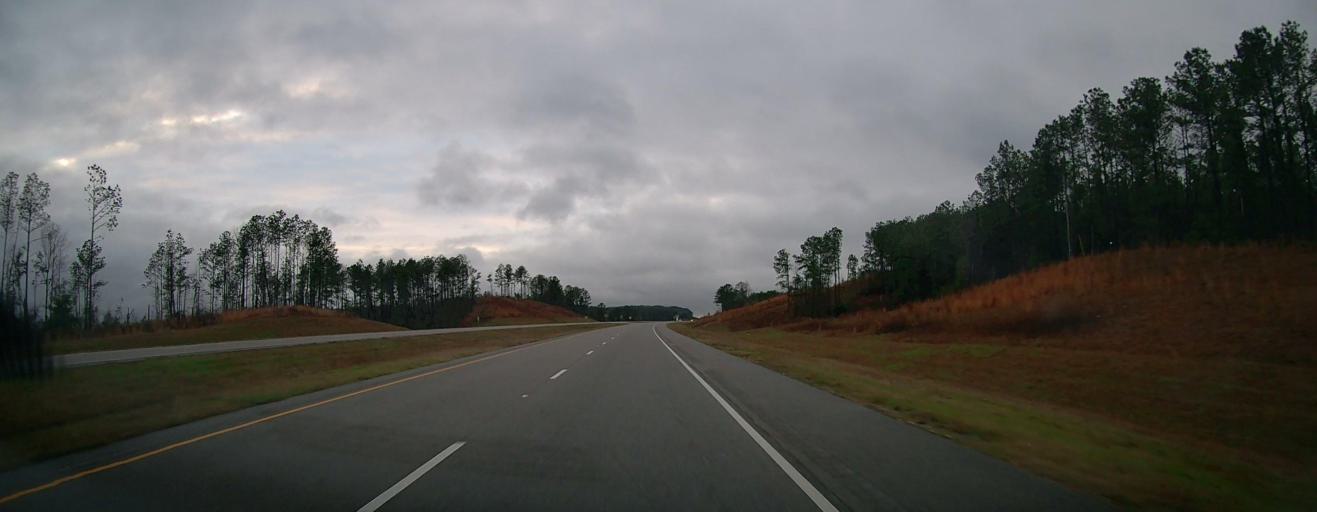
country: US
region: Alabama
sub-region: Bibb County
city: Centreville
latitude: 32.9463
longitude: -87.0933
